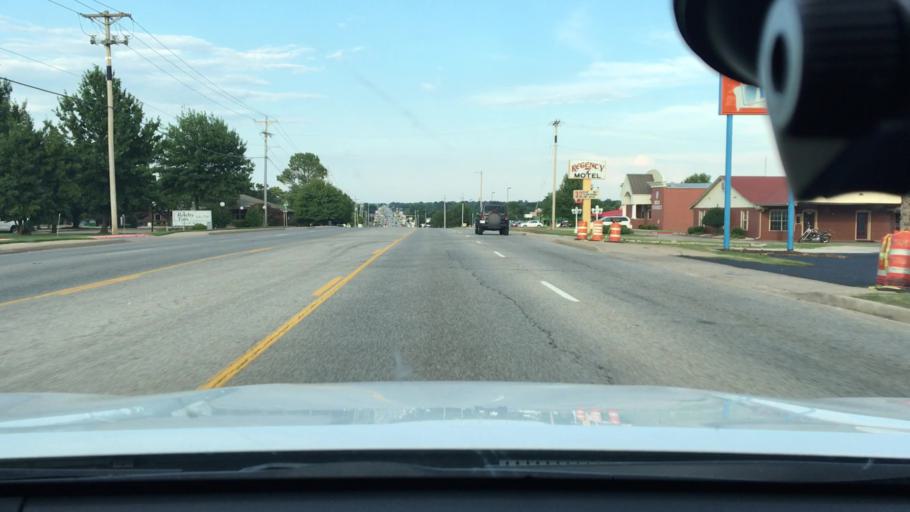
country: US
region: Arkansas
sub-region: Benton County
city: Rogers
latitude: 36.3347
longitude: -94.1711
